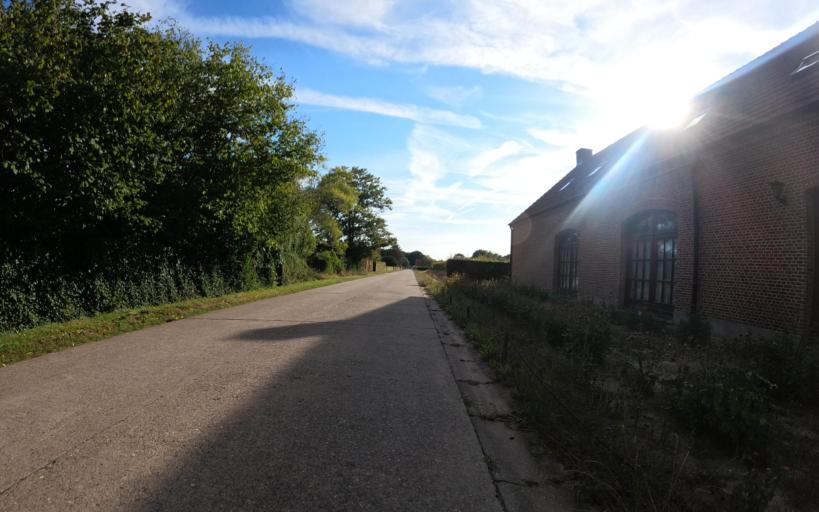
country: BE
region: Flanders
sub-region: Provincie Antwerpen
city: Zandhoven
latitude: 51.2271
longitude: 4.6359
